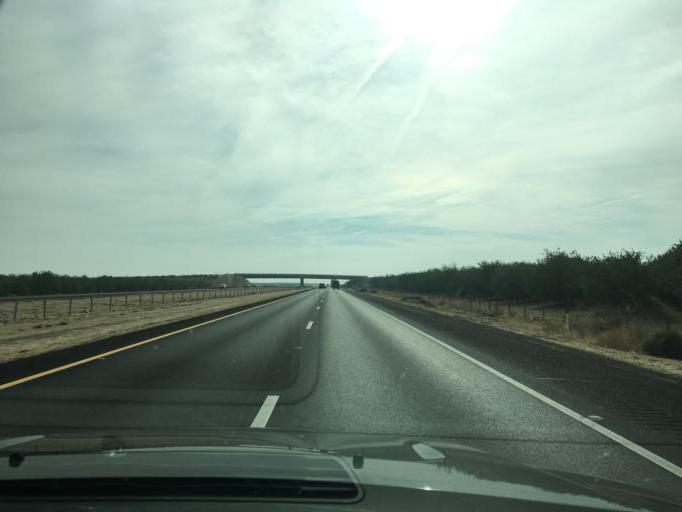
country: US
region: California
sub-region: Fresno County
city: Huron
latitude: 36.2061
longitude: -120.2138
